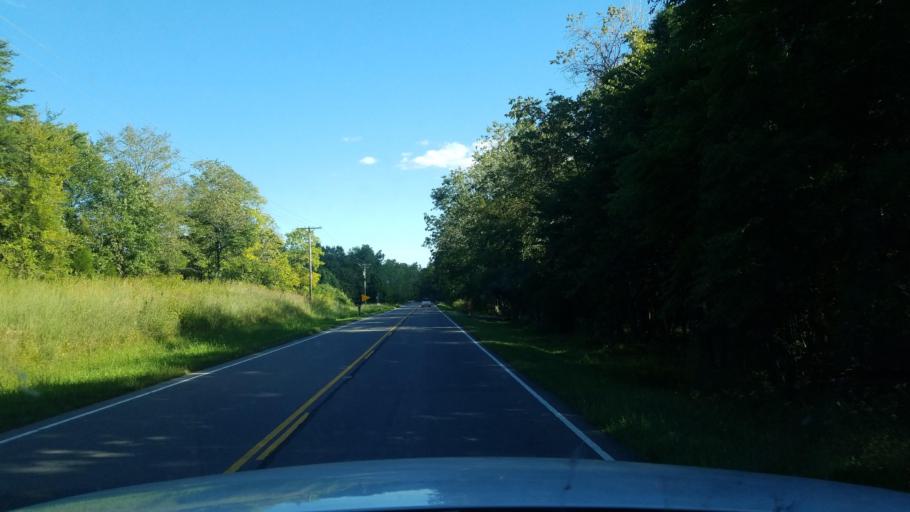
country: US
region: Illinois
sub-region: Saline County
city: Harrisburg
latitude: 37.6051
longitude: -88.4614
